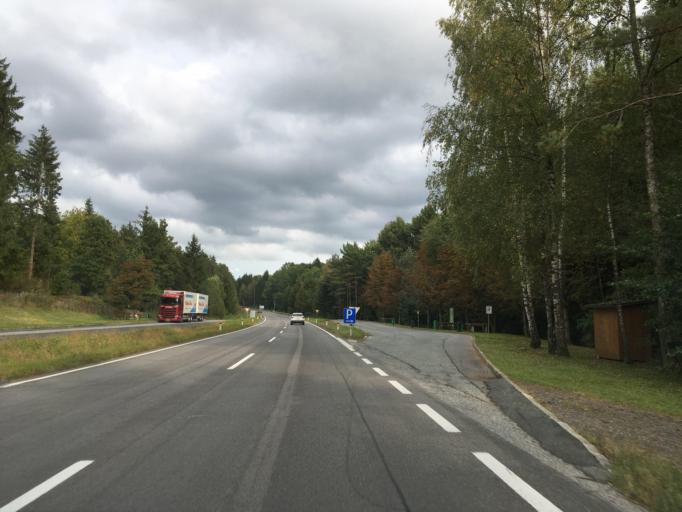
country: AT
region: Styria
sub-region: Politischer Bezirk Hartberg-Fuerstenfeld
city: Friedberg
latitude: 47.4168
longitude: 16.0400
